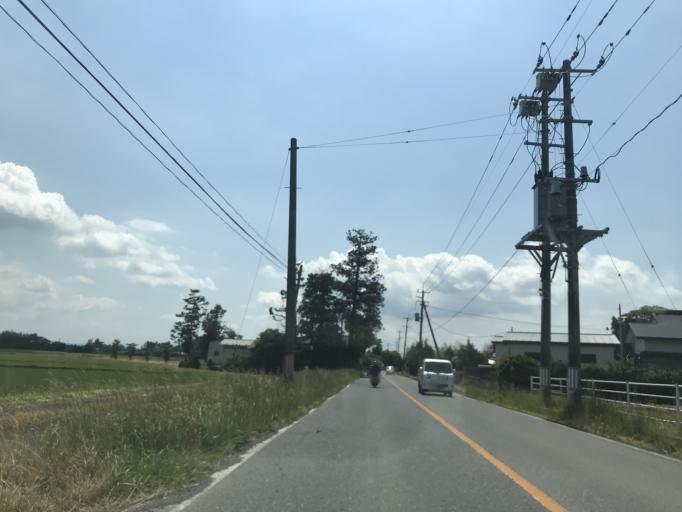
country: JP
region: Miyagi
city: Kogota
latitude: 38.5750
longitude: 141.0352
